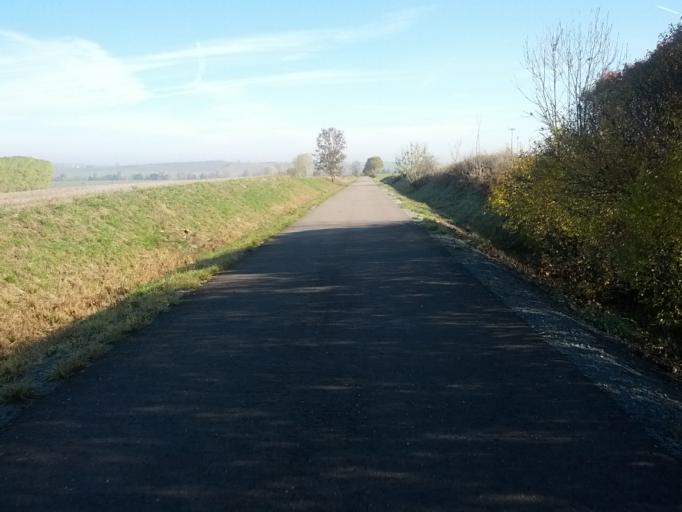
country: DE
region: Thuringia
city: Haina
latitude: 50.9959
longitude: 10.5028
